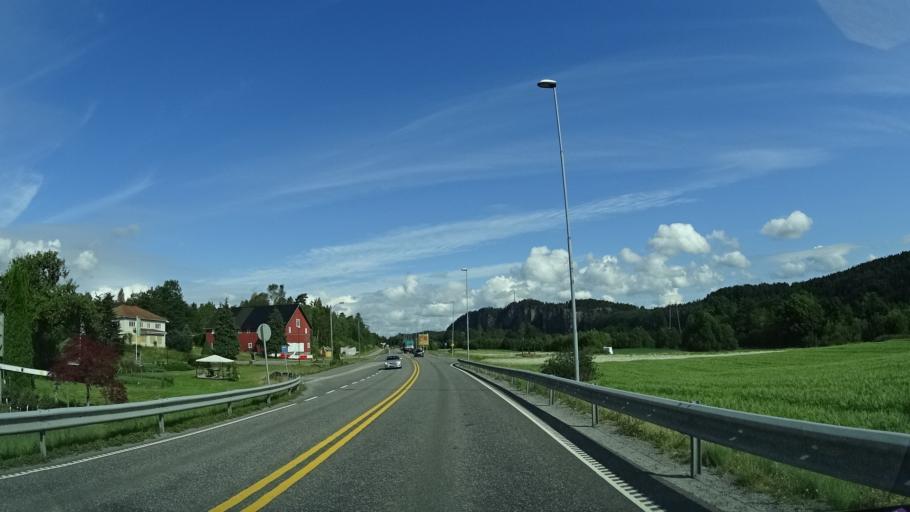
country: NO
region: Telemark
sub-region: Bamble
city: Langesund
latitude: 59.0286
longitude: 9.6801
